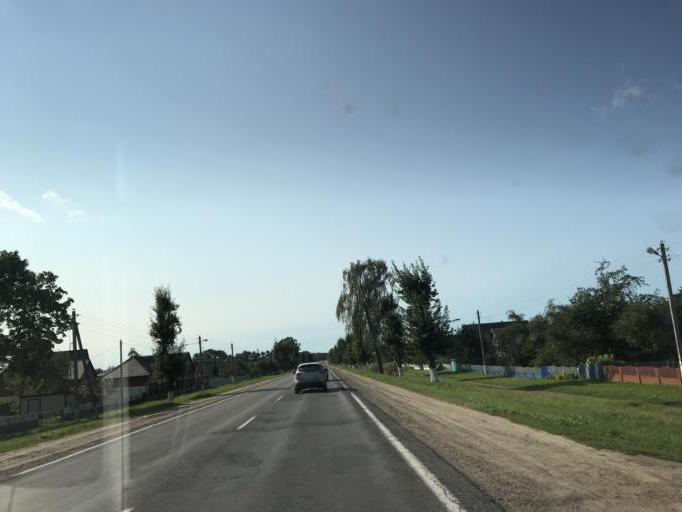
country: BY
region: Mogilev
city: Buynichy
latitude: 53.8350
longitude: 30.2458
